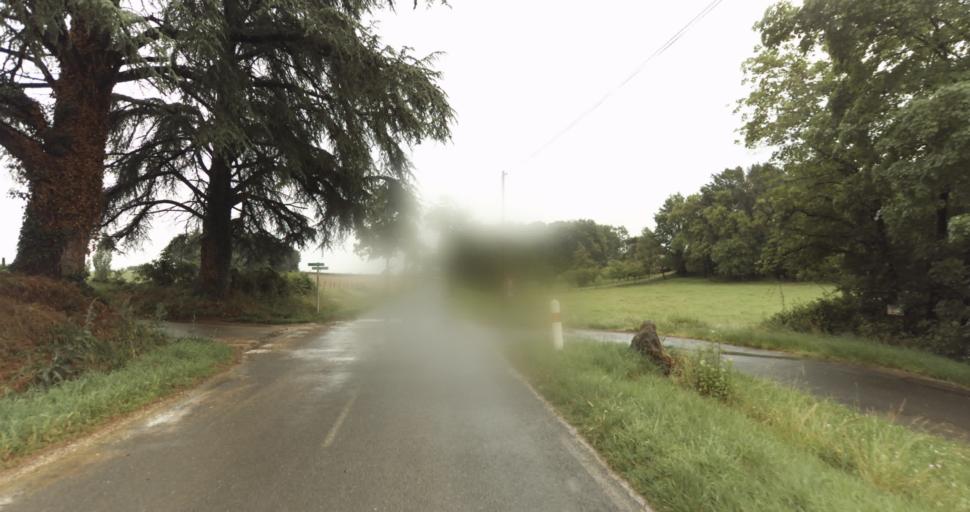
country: FR
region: Aquitaine
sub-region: Departement de la Dordogne
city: Beaumont-du-Perigord
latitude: 44.7784
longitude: 0.8218
